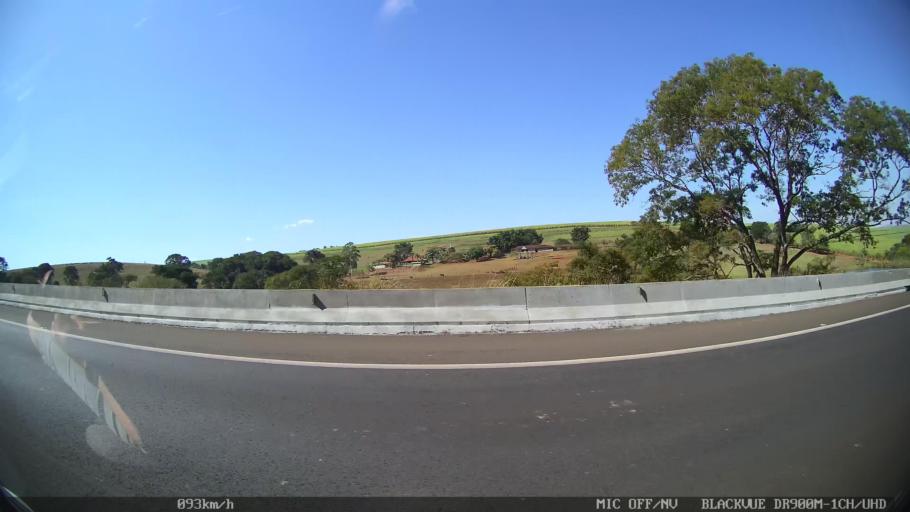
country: BR
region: Sao Paulo
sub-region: Franca
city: Franca
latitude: -20.7011
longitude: -47.5012
